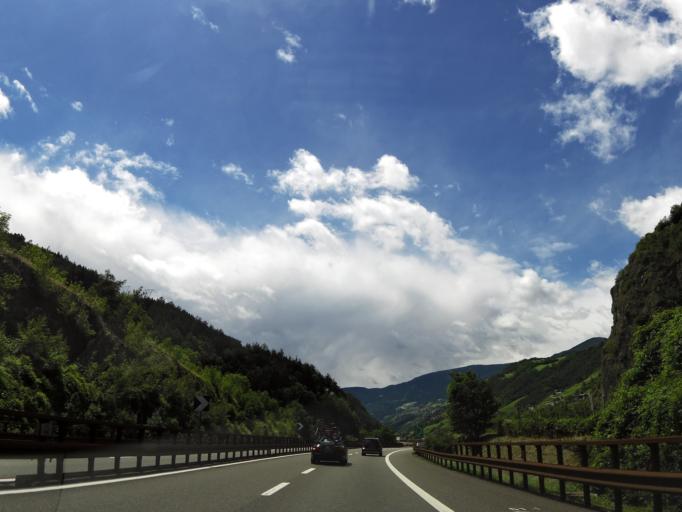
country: IT
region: Trentino-Alto Adige
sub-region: Bolzano
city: Velturno
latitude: 46.6586
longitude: 11.6059
